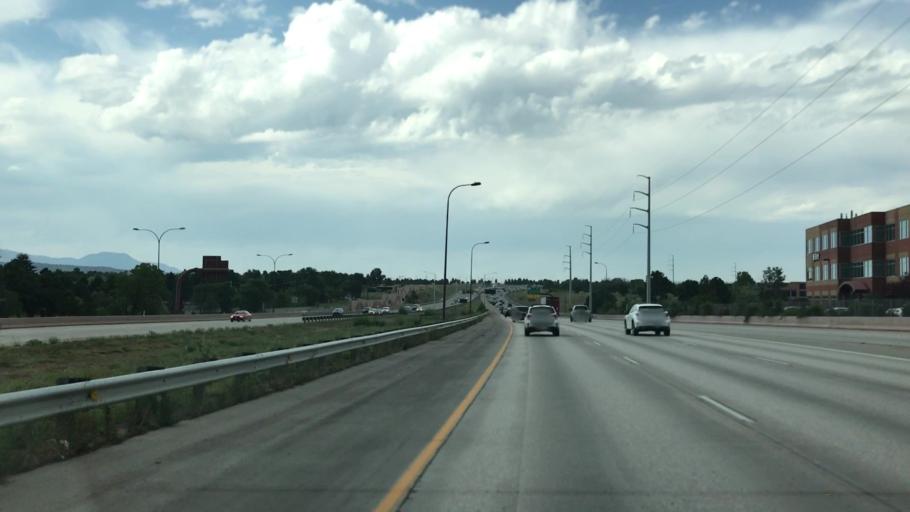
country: US
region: Colorado
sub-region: El Paso County
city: Air Force Academy
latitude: 38.9367
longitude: -104.8125
